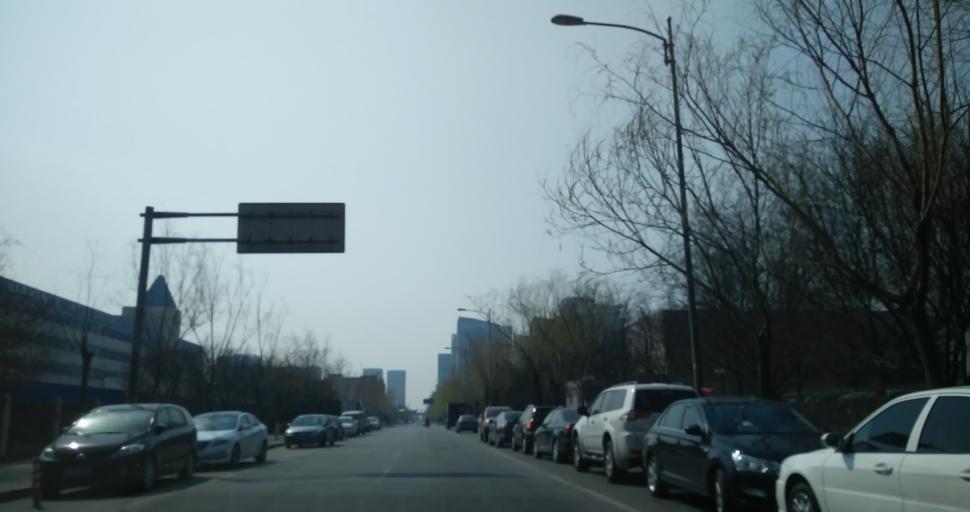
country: CN
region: Beijing
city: Jiugong
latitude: 39.7935
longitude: 116.5166
